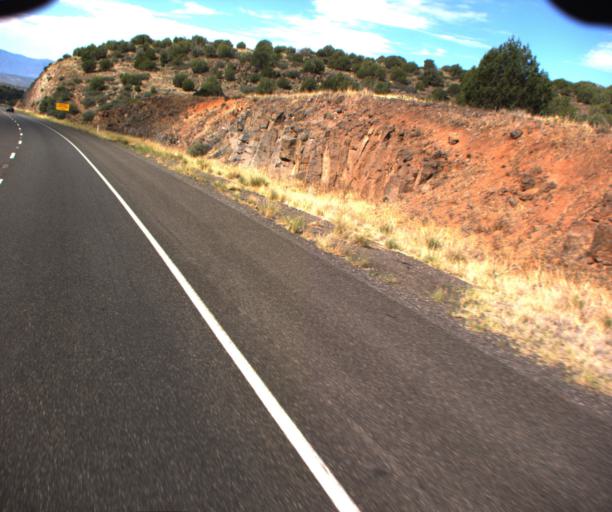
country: US
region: Arizona
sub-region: Yavapai County
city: Big Park
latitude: 34.7189
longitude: -111.7256
